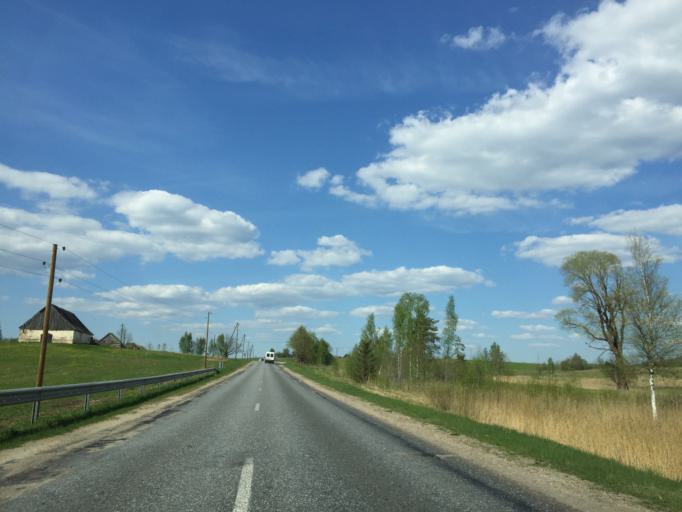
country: LV
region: Limbazu Rajons
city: Limbazi
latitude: 57.4453
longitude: 24.7242
